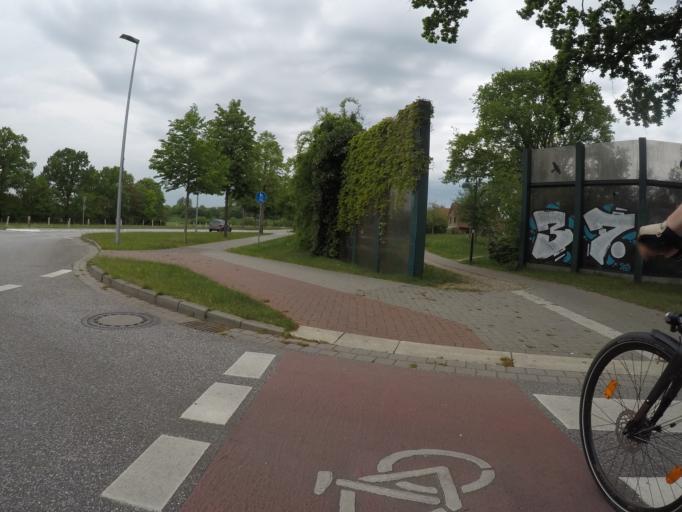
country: DE
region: Schleswig-Holstein
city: Norderstedt
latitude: 53.7021
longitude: 9.9761
